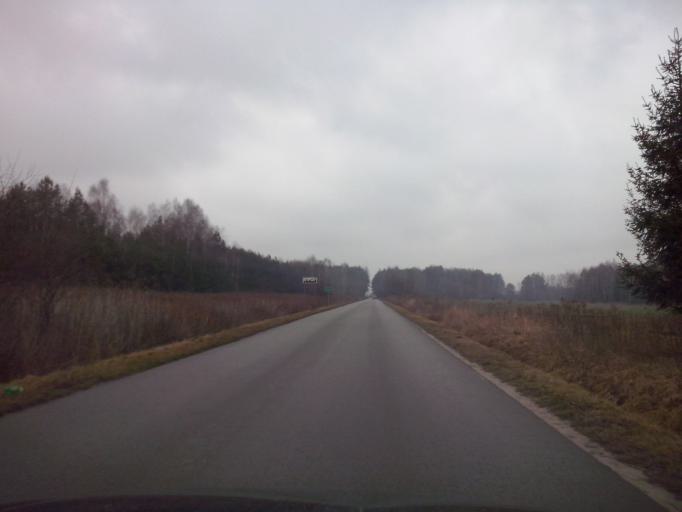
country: PL
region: Subcarpathian Voivodeship
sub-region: Powiat nizanski
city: Bieliny
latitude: 50.4517
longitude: 22.2859
